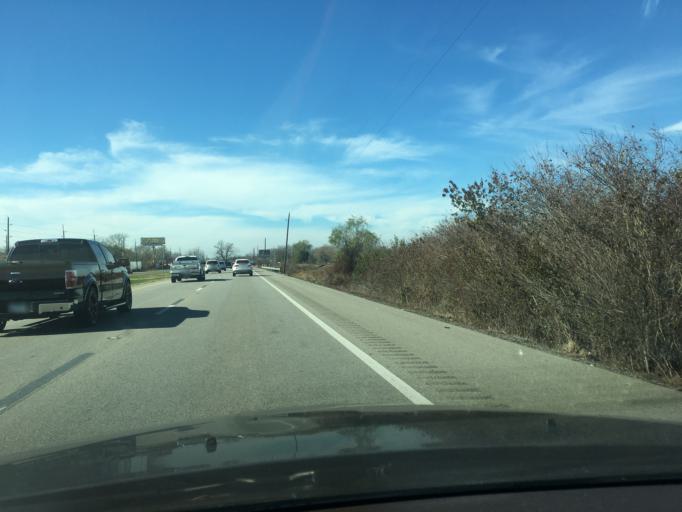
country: US
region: Texas
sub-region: Fort Bend County
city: Pecan Grove
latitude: 29.5972
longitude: -95.7285
